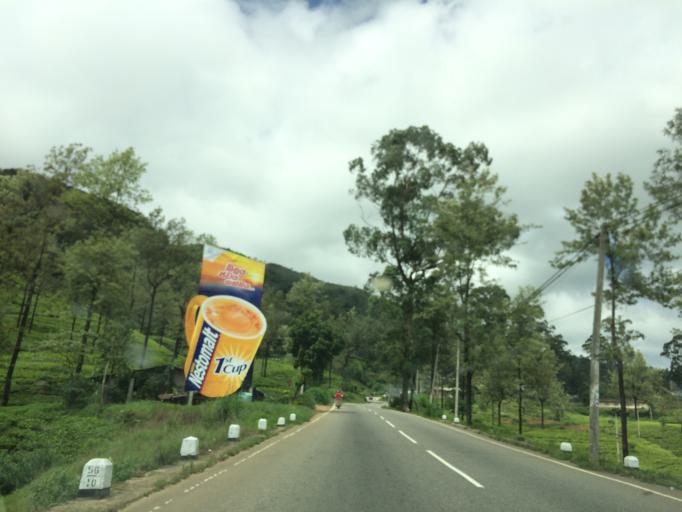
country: LK
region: Central
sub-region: Nuwara Eliya District
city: Nuwara Eliya
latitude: 7.0209
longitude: 80.7238
